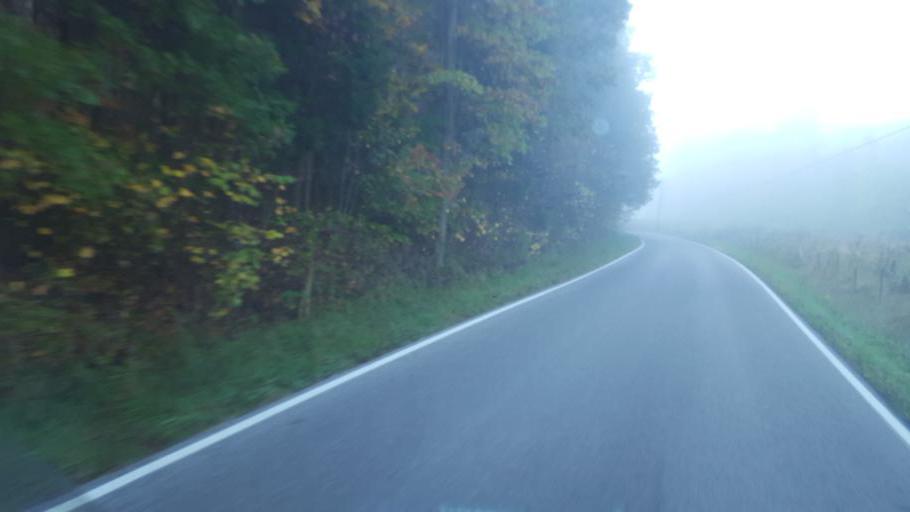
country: US
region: Ohio
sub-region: Adams County
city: Manchester
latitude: 38.5009
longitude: -83.5539
